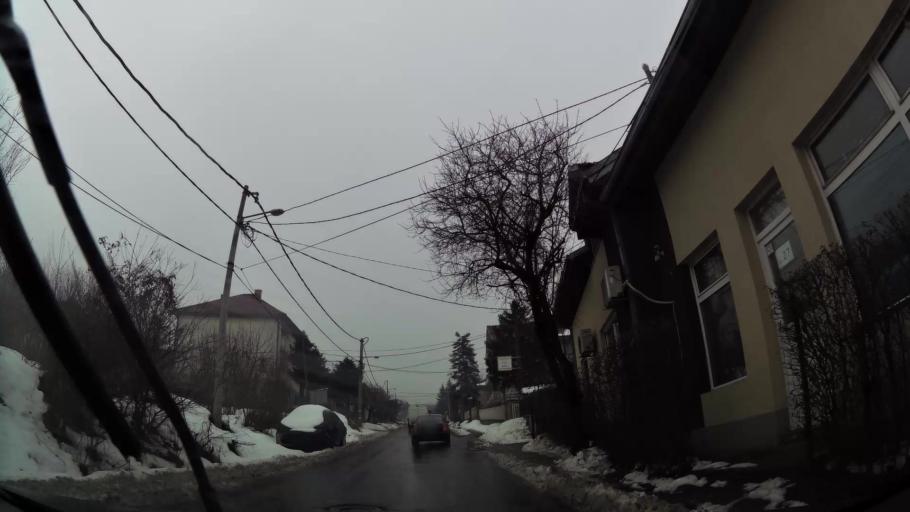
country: RS
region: Central Serbia
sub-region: Belgrade
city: Zvezdara
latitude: 44.7742
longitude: 20.5284
